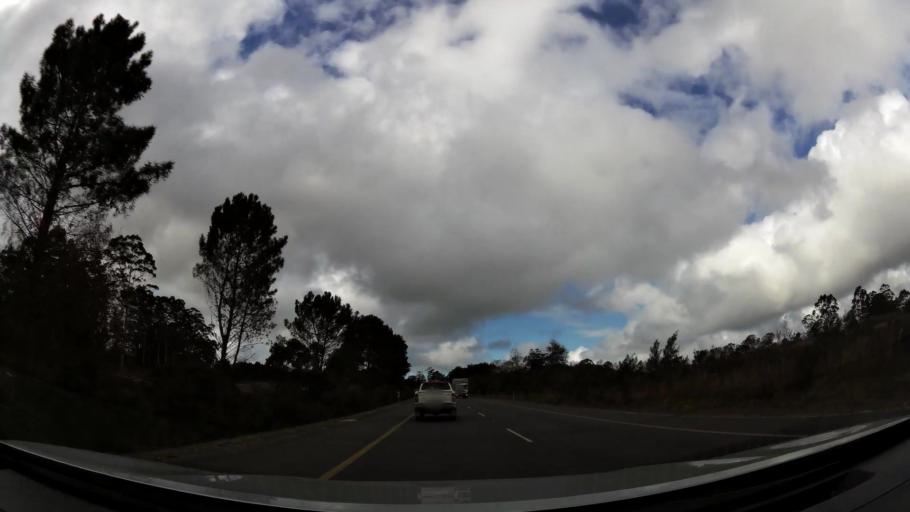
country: ZA
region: Western Cape
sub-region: Eden District Municipality
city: Plettenberg Bay
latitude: -34.0431
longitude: 23.2594
